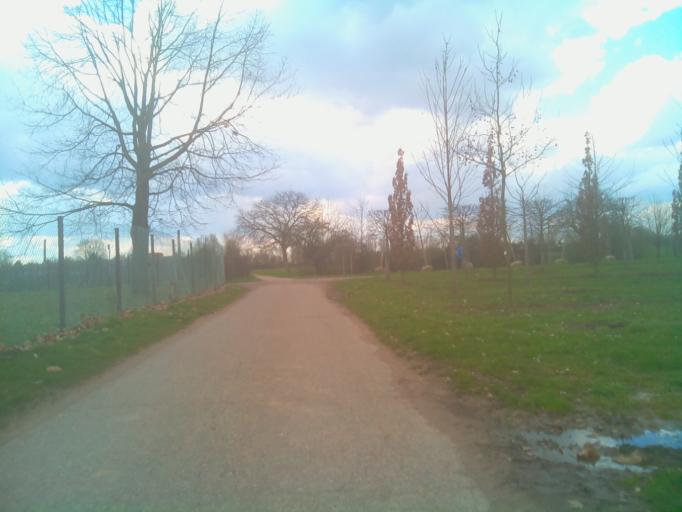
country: DE
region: Baden-Wuerttemberg
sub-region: Karlsruhe Region
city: Ladenburg
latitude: 49.4767
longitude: 8.6353
